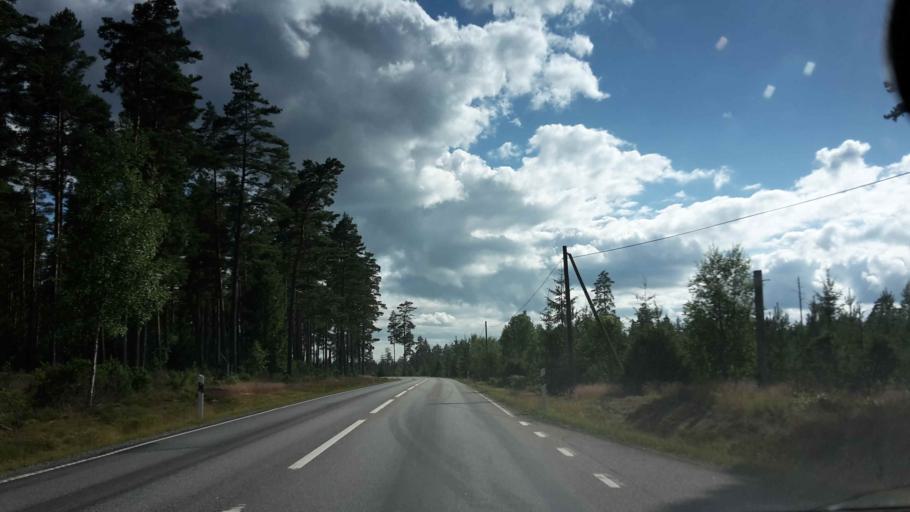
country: SE
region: OErebro
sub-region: Hallsbergs Kommun
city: Palsboda
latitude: 58.8614
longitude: 15.4109
